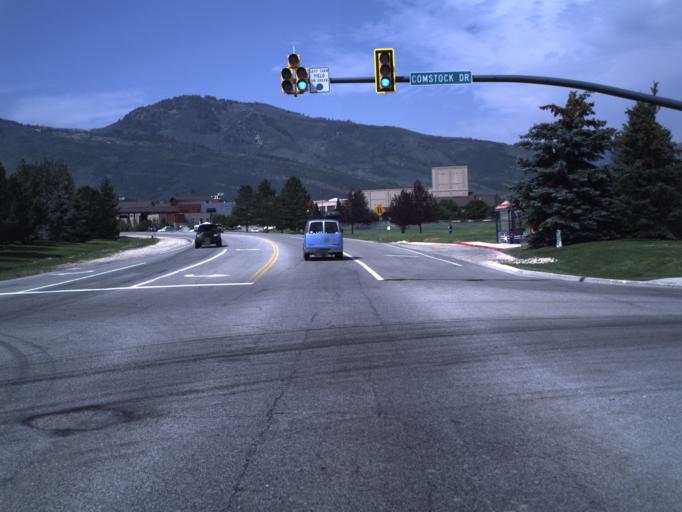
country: US
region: Utah
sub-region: Summit County
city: Park City
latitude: 40.6680
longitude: -111.4919
